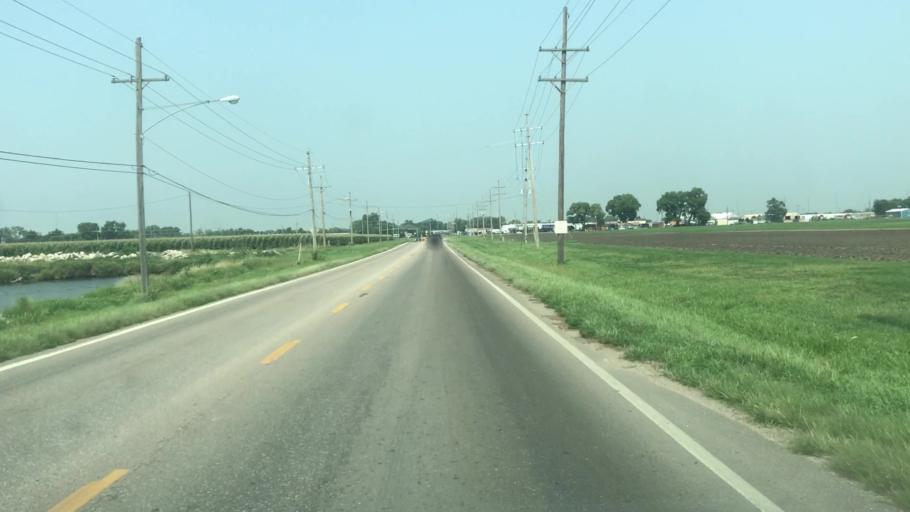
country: US
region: Nebraska
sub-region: Hall County
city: Grand Island
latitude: 40.9264
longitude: -98.3206
